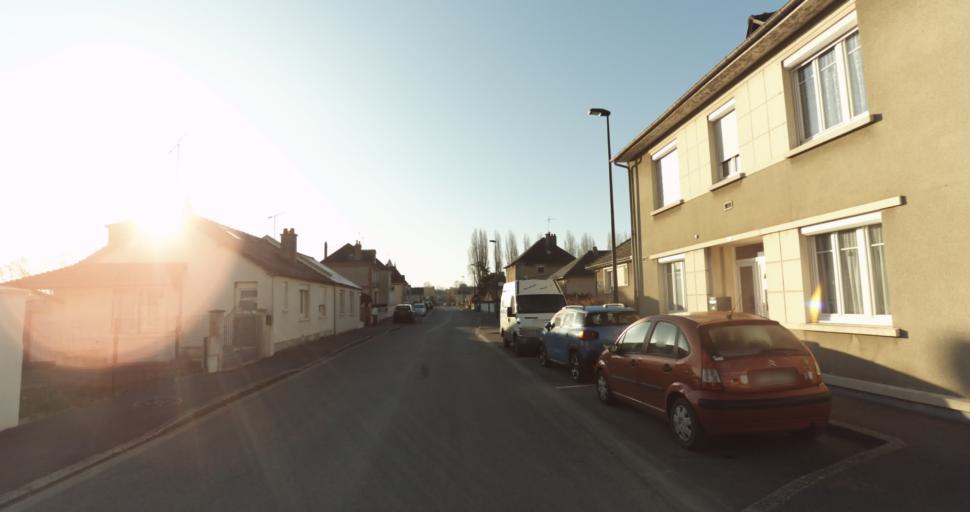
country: FR
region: Lower Normandy
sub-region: Departement du Calvados
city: Saint-Pierre-sur-Dives
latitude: 49.0223
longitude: -0.0389
